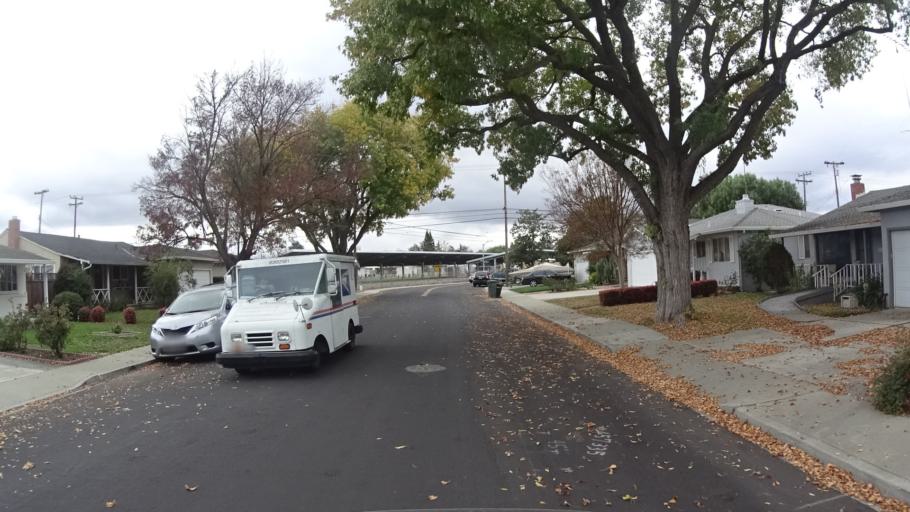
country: US
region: California
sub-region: Santa Clara County
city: Santa Clara
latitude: 37.3339
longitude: -121.9752
